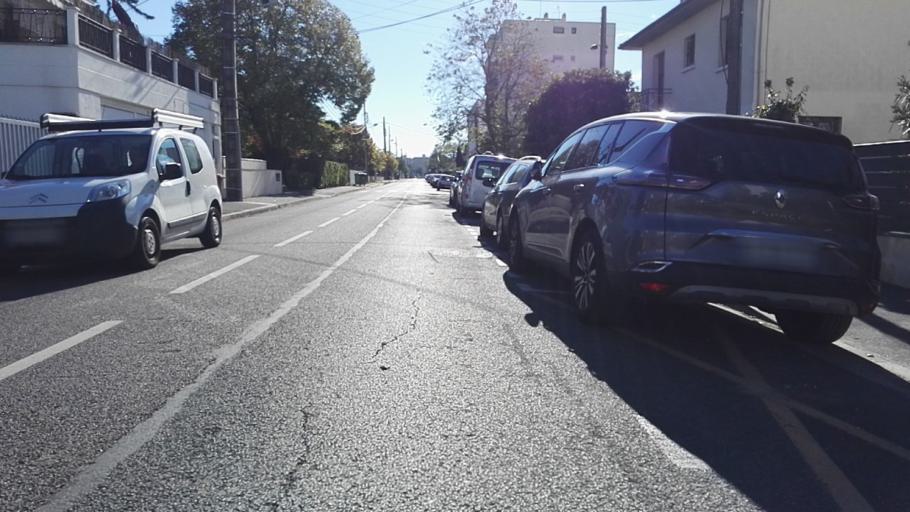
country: FR
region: Aquitaine
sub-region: Departement de la Gironde
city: Bruges
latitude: 44.8625
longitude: -0.6189
